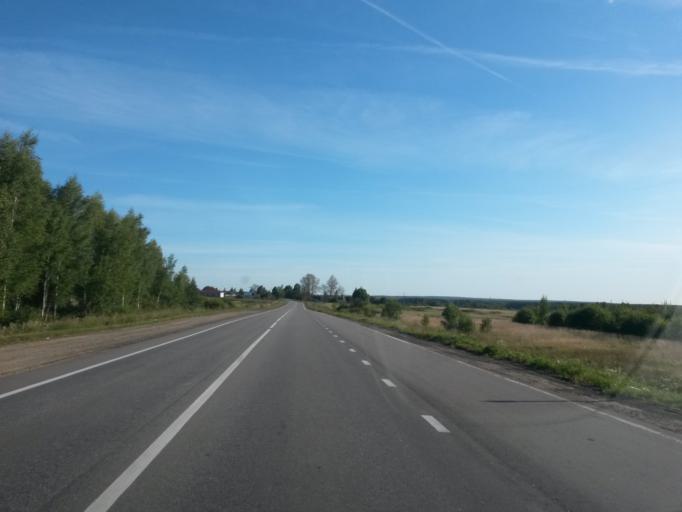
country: RU
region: Jaroslavl
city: Gavrilov-Yam
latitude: 57.3582
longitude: 39.9082
